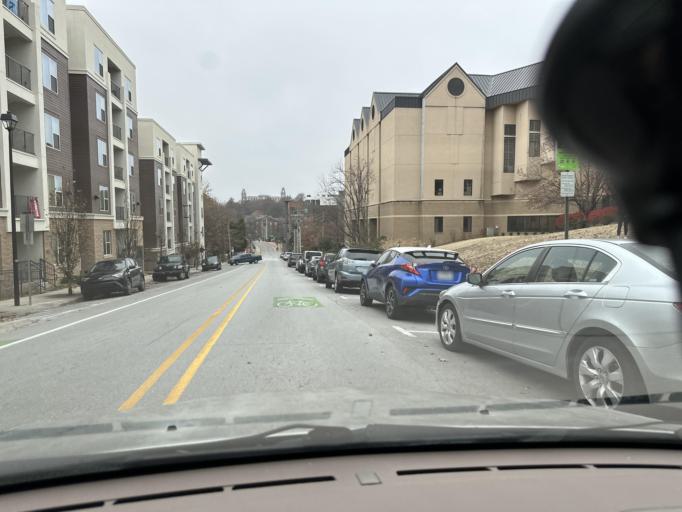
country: US
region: Arkansas
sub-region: Washington County
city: Fayetteville
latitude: 36.0686
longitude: -94.1634
